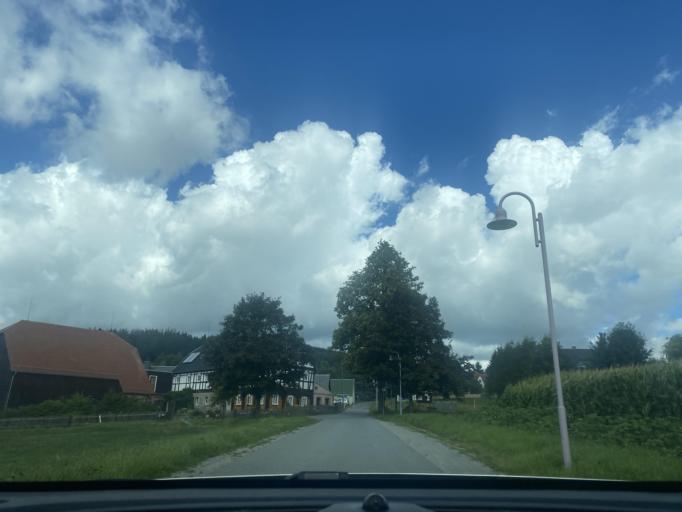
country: DE
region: Saxony
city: Beiersdorf
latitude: 51.0758
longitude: 14.5309
